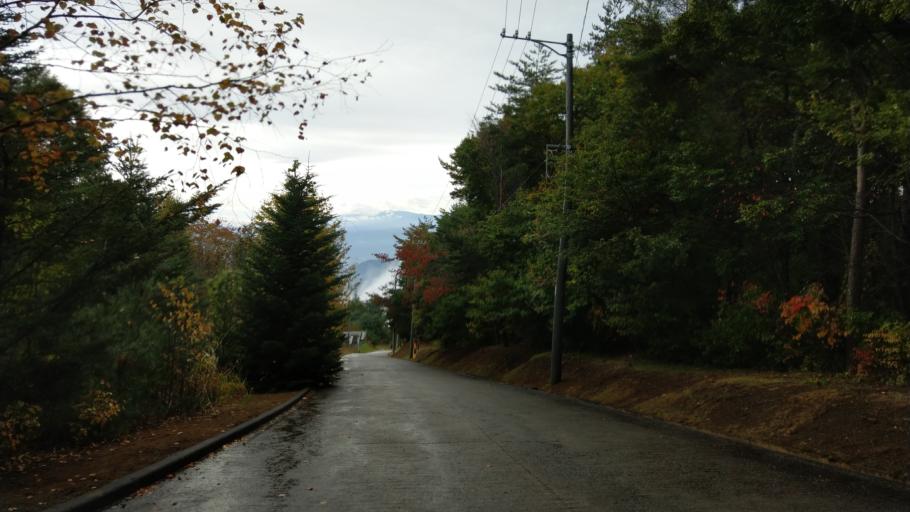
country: JP
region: Nagano
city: Komoro
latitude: 36.3659
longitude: 138.4267
